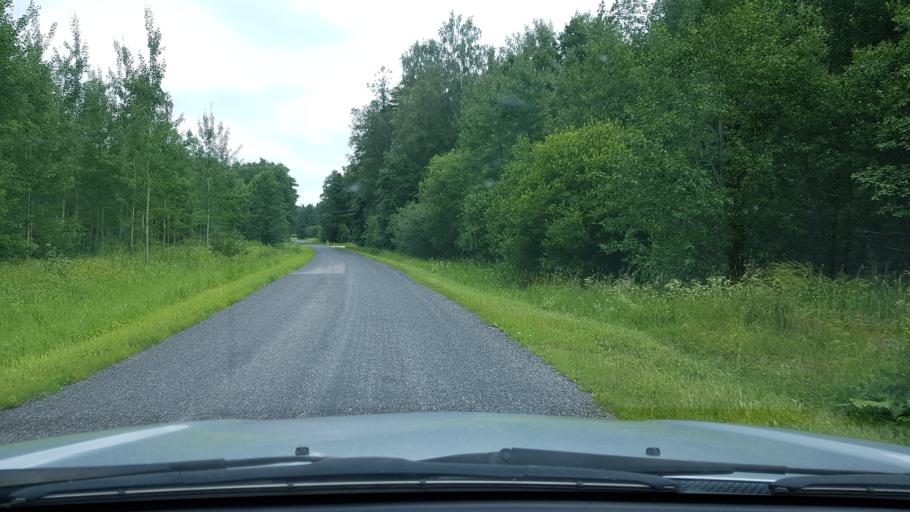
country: EE
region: Ida-Virumaa
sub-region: Narva-Joesuu linn
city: Narva-Joesuu
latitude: 59.3534
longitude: 28.0371
